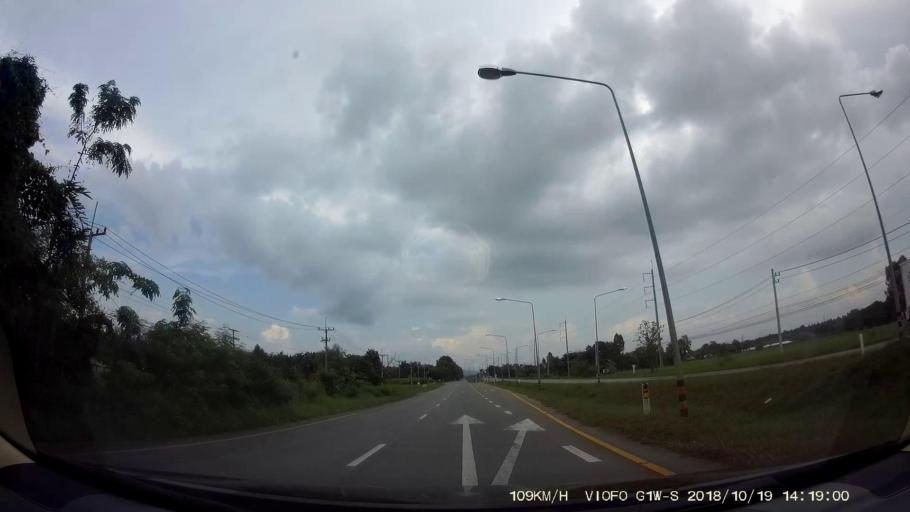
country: TH
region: Chaiyaphum
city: Kaeng Khro
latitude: 16.0226
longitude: 102.2410
